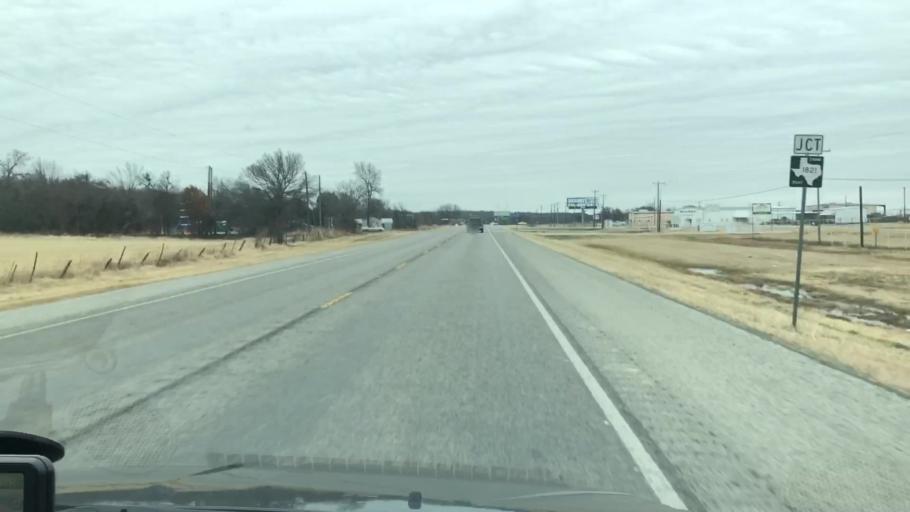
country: US
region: Texas
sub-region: Palo Pinto County
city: Mineral Wells
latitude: 32.8507
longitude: -98.0971
